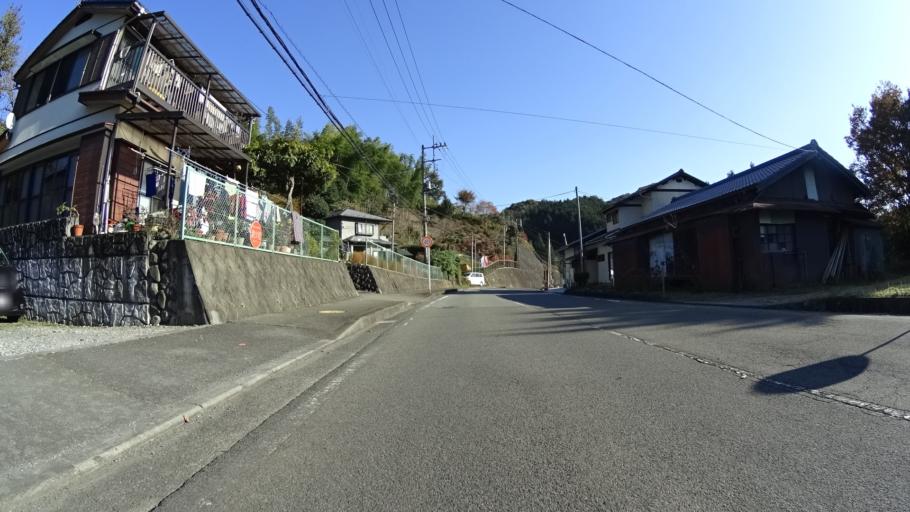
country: JP
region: Yamanashi
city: Uenohara
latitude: 35.6427
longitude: 139.1271
